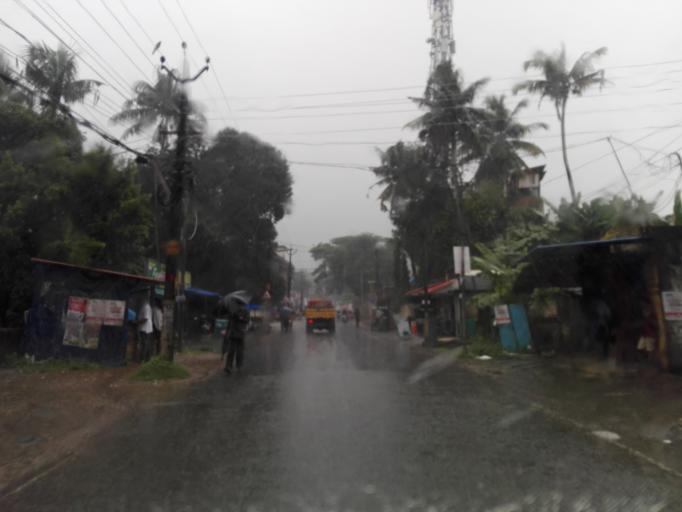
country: IN
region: Kerala
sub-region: Ernakulam
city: Elur
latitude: 10.0783
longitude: 76.3199
